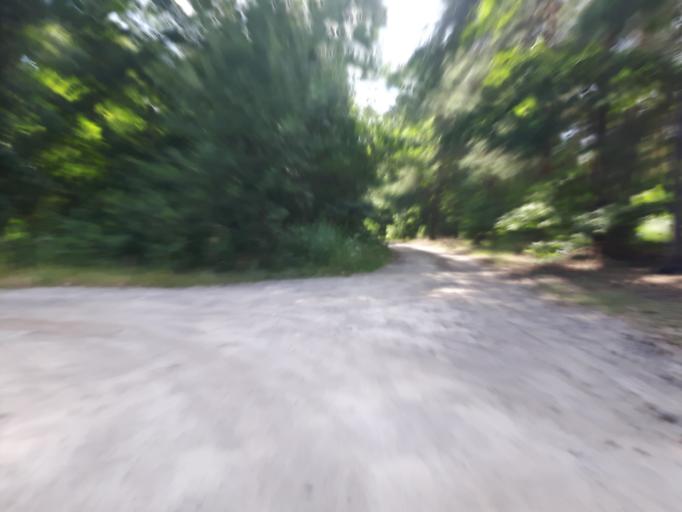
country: PL
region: Masovian Voivodeship
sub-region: Powiat wolominski
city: Zabki
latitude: 52.2948
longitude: 21.1305
